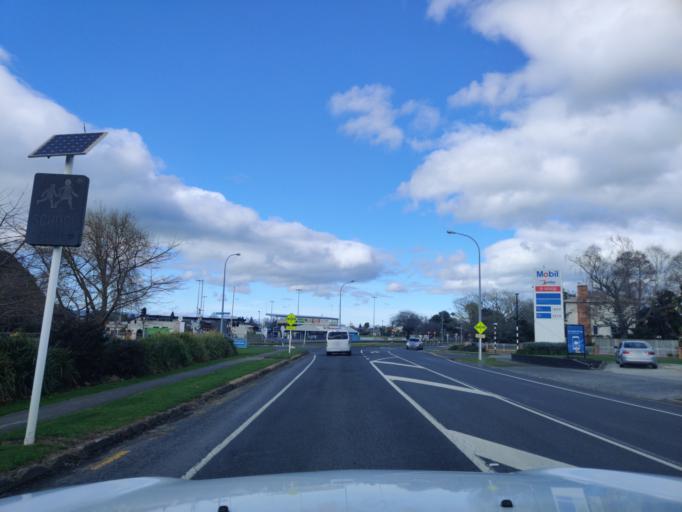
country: NZ
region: Waikato
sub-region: Matamata-Piako District
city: Matamata
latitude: -37.8141
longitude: 175.7708
